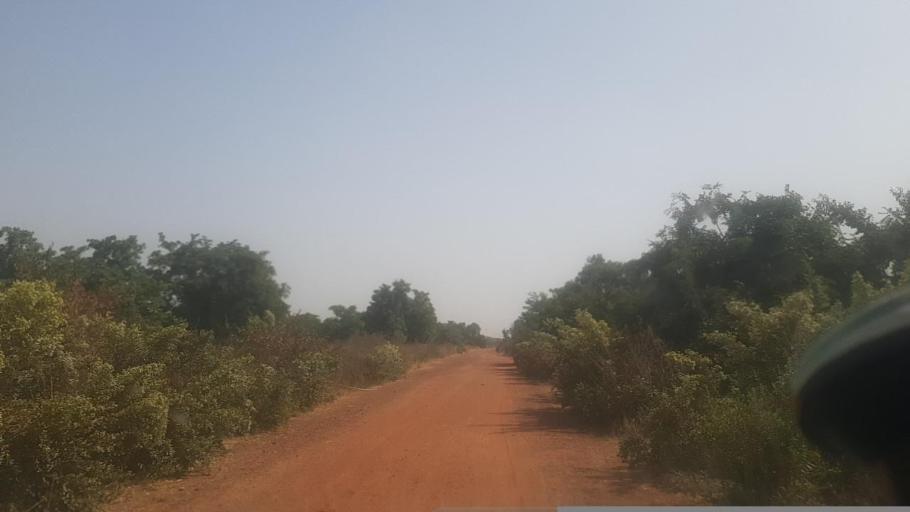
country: ML
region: Segou
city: Bla
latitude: 12.9178
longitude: -6.2545
